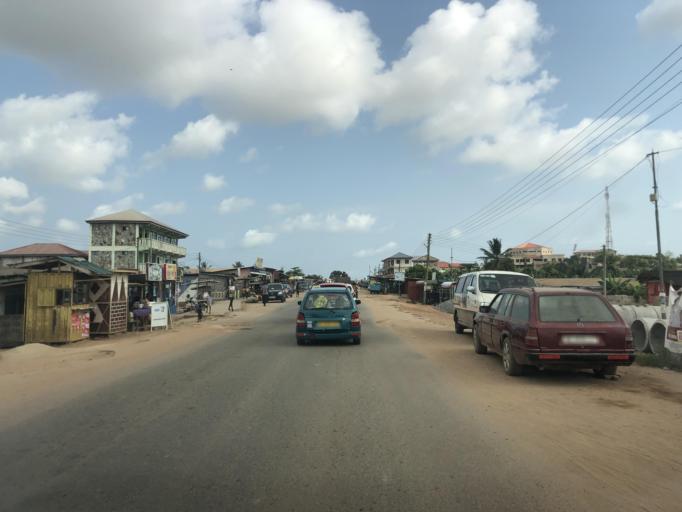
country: GH
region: Central
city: Cape Coast
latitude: 5.1438
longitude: -1.2854
